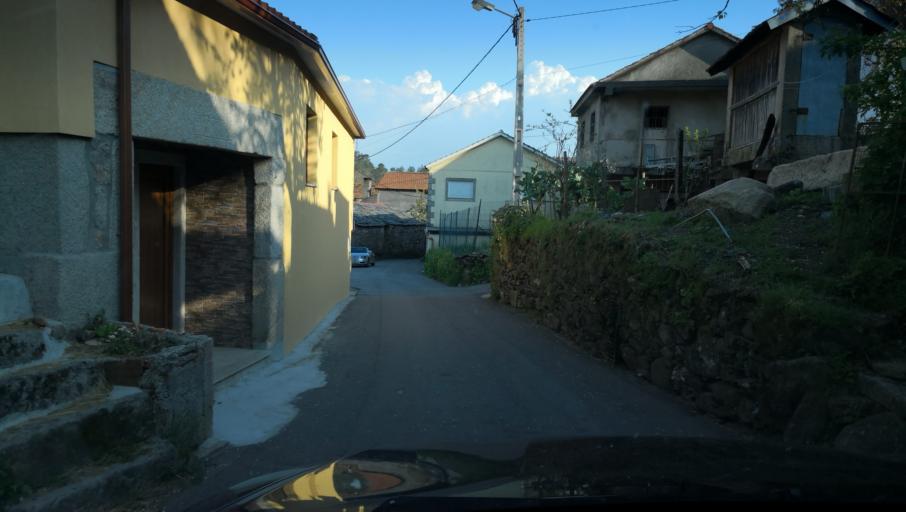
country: PT
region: Vila Real
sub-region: Vila Real
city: Vila Real
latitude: 41.2997
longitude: -7.8371
